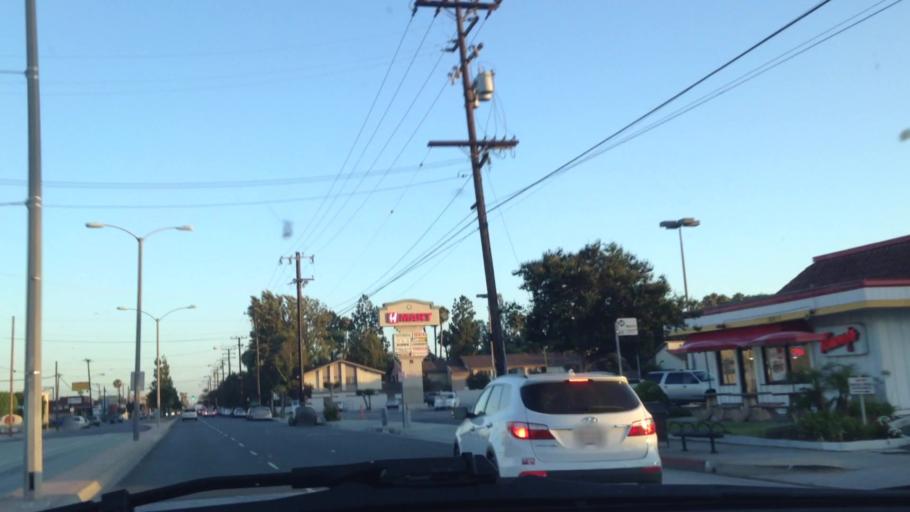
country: US
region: California
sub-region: Los Angeles County
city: Norwalk
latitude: 33.8875
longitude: -118.0825
